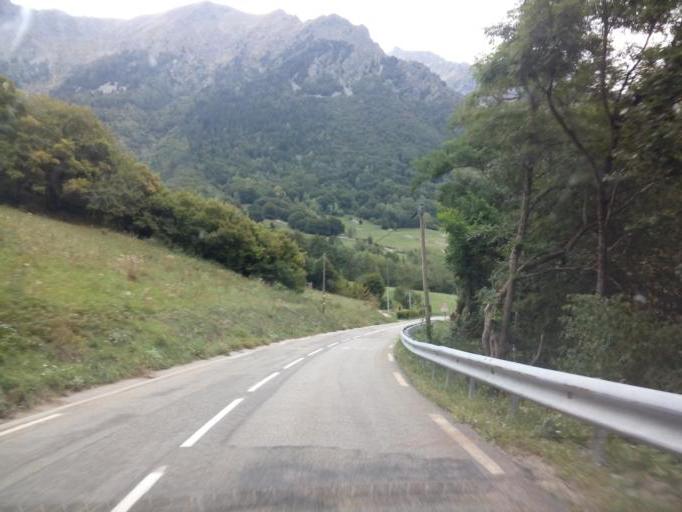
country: FR
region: Rhone-Alpes
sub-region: Departement de l'Isere
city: Vaulnaveys-le-Bas
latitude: 45.0070
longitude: 5.8745
